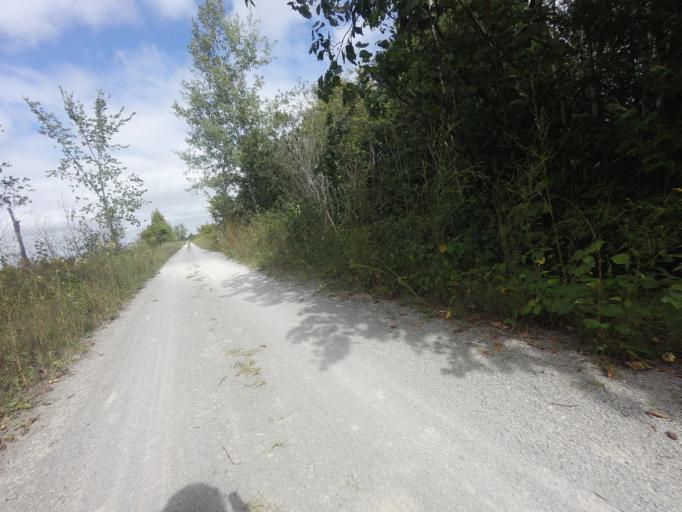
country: CA
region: Ontario
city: Uxbridge
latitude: 44.1702
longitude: -79.0763
